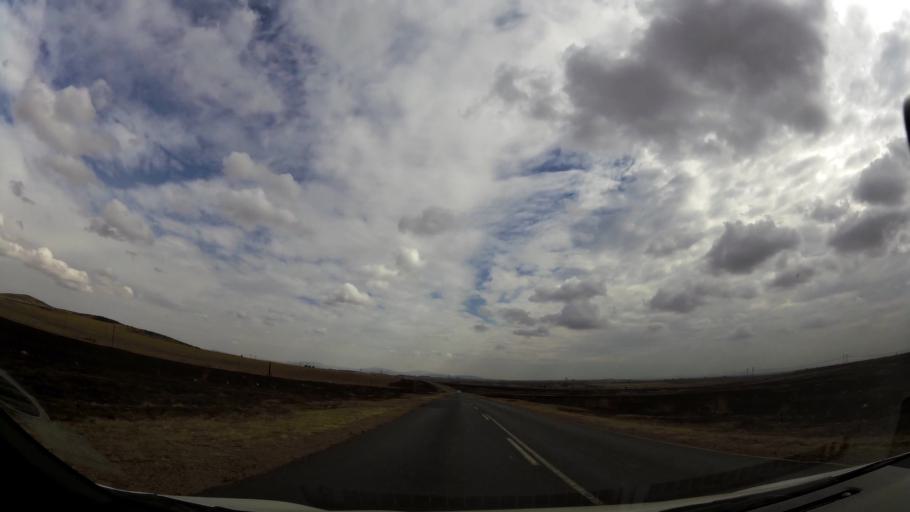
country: ZA
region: Gauteng
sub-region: Sedibeng District Municipality
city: Heidelberg
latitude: -26.4345
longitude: 28.2098
